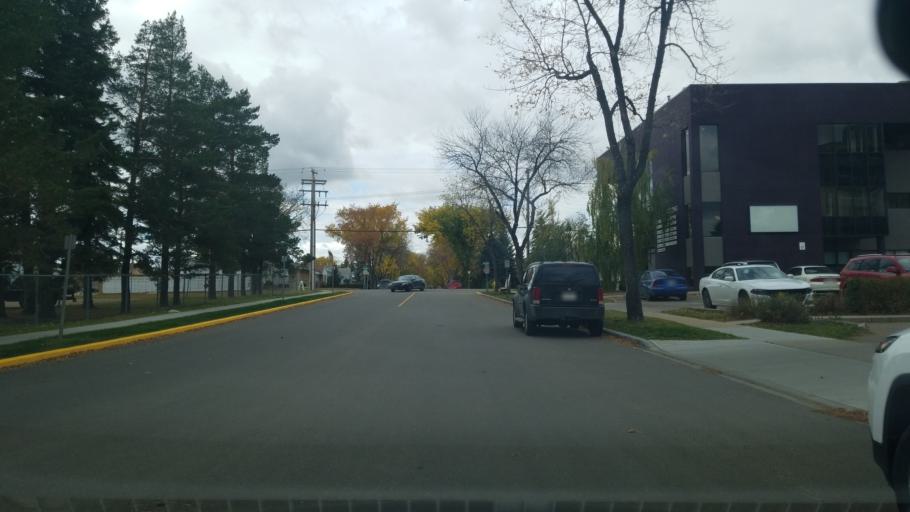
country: CA
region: Saskatchewan
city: Lloydminster
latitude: 53.2798
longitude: -110.0094
